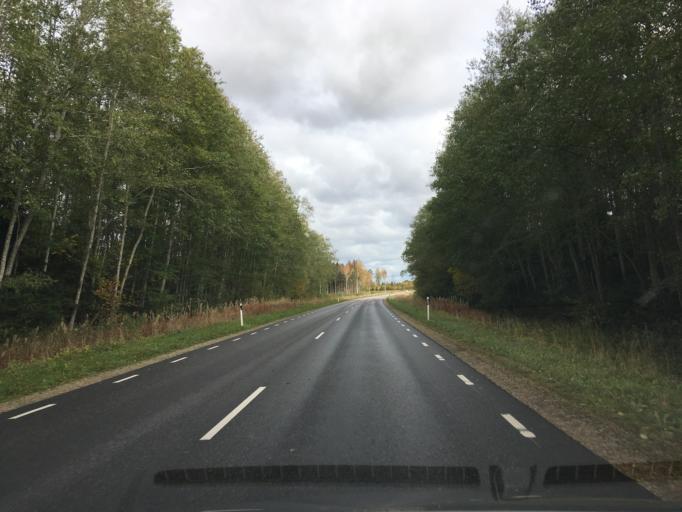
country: EE
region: Harju
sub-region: Anija vald
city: Kehra
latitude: 59.2426
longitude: 25.2976
